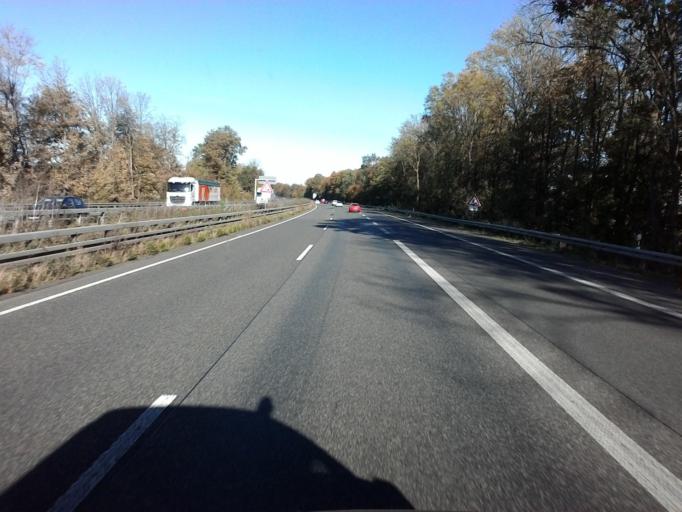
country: BE
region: Wallonia
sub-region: Province de Liege
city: Raeren
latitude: 50.7231
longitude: 6.1293
